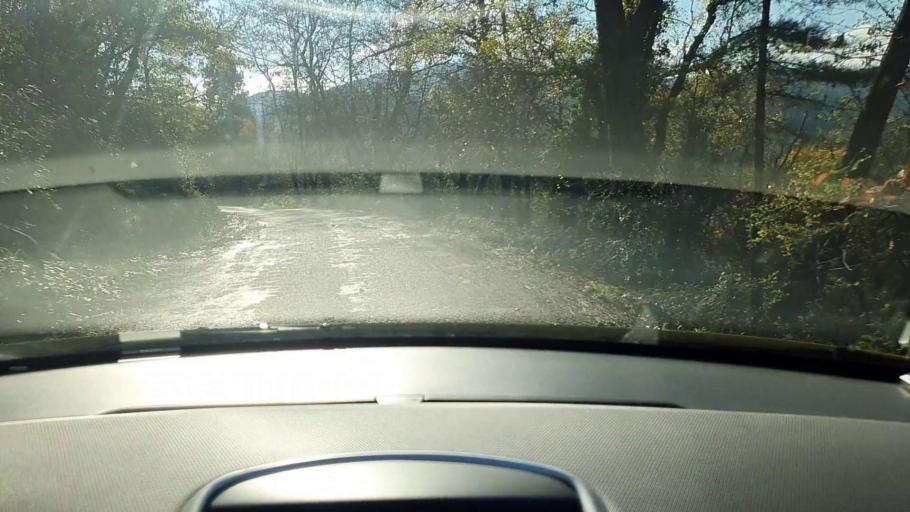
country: FR
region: Languedoc-Roussillon
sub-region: Departement du Gard
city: Branoux-les-Taillades
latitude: 44.2562
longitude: 3.9770
